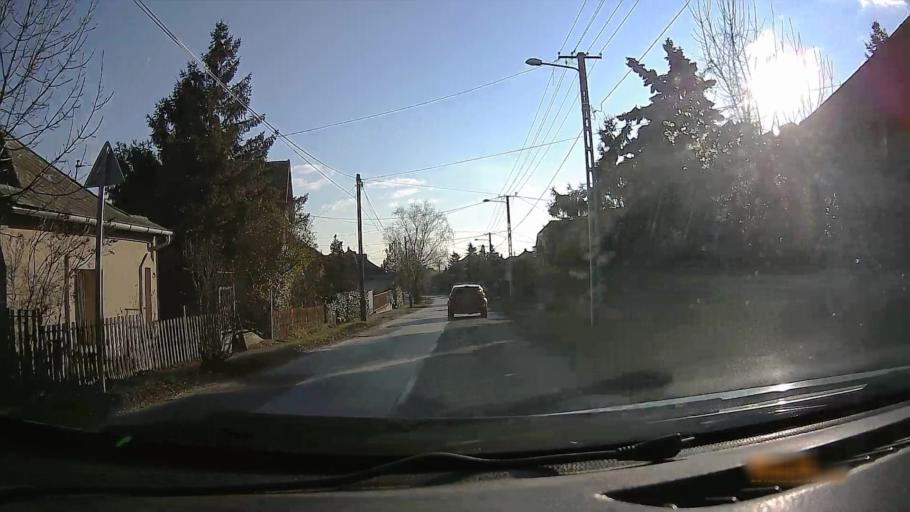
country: HU
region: Heves
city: Domoszlo
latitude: 47.8272
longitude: 20.1114
